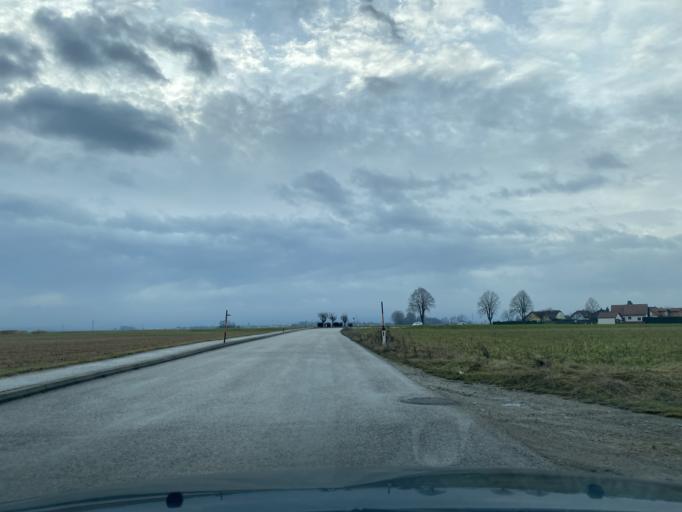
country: AT
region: Lower Austria
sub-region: Politischer Bezirk Sankt Polten
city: Prinzersdorf
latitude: 48.1991
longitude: 15.5081
